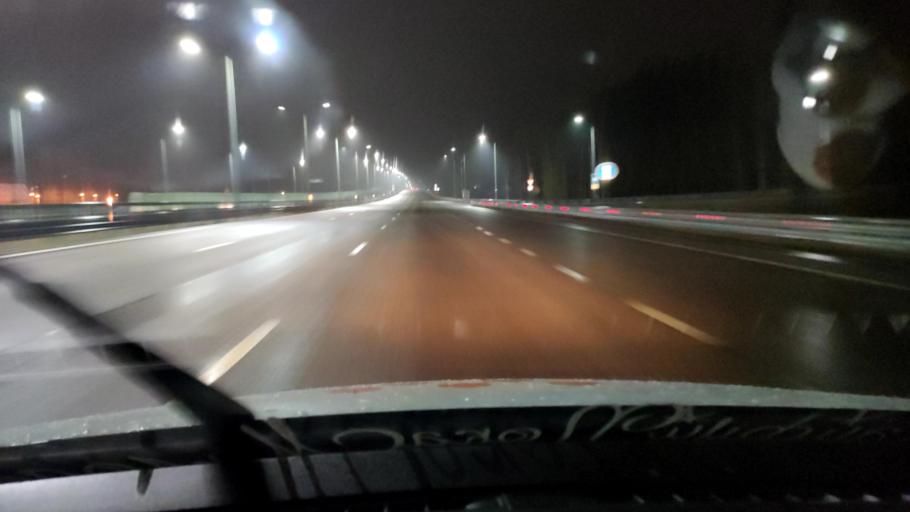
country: RU
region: Voronezj
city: Somovo
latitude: 51.7419
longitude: 39.3073
